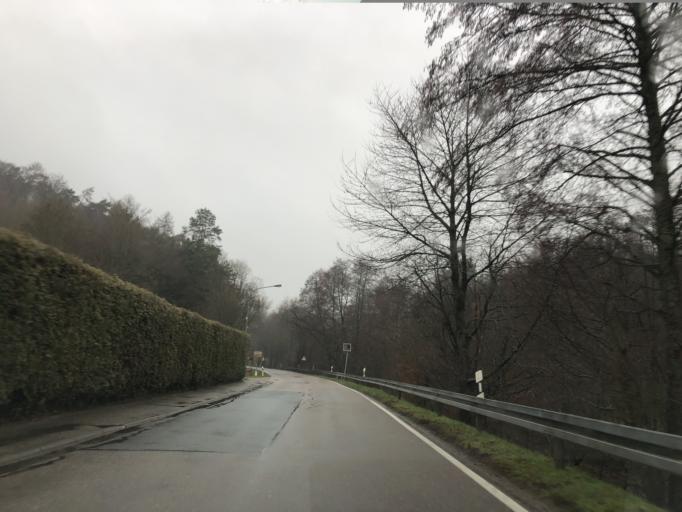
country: DE
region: Hesse
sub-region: Regierungsbezirk Darmstadt
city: Lutzelbach
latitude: 49.7812
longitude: 9.1141
